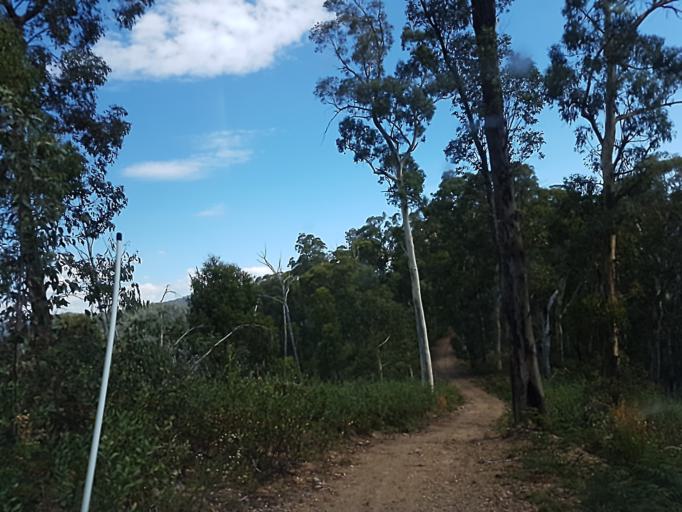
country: AU
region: Victoria
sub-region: Alpine
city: Mount Beauty
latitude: -36.9175
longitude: 146.9987
